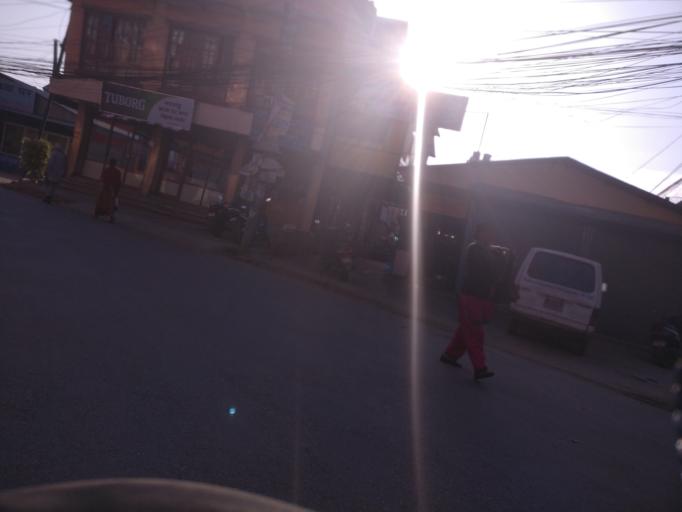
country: NP
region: Central Region
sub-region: Bagmati Zone
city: Patan
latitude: 27.6573
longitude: 85.3196
